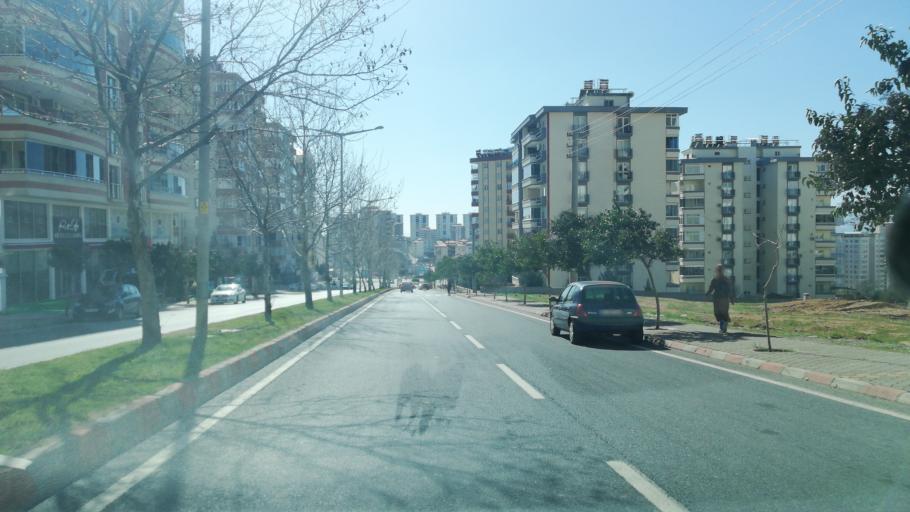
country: TR
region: Kahramanmaras
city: Kahramanmaras
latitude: 37.5854
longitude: 36.8790
